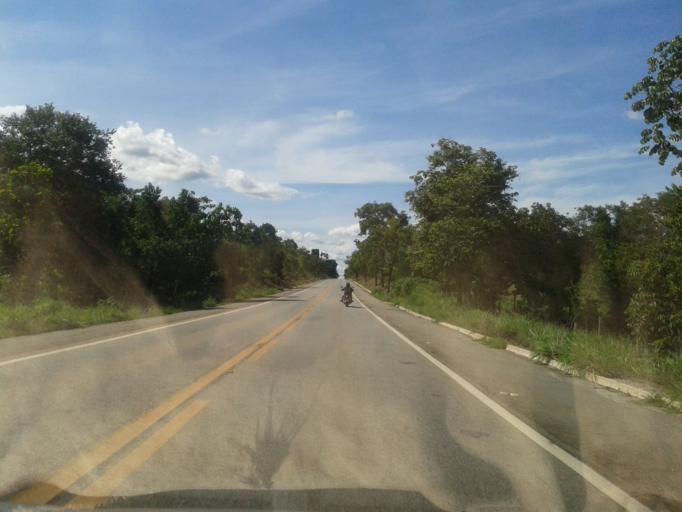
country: BR
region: Goias
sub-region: Mozarlandia
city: Mozarlandia
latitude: -15.2869
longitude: -50.4710
